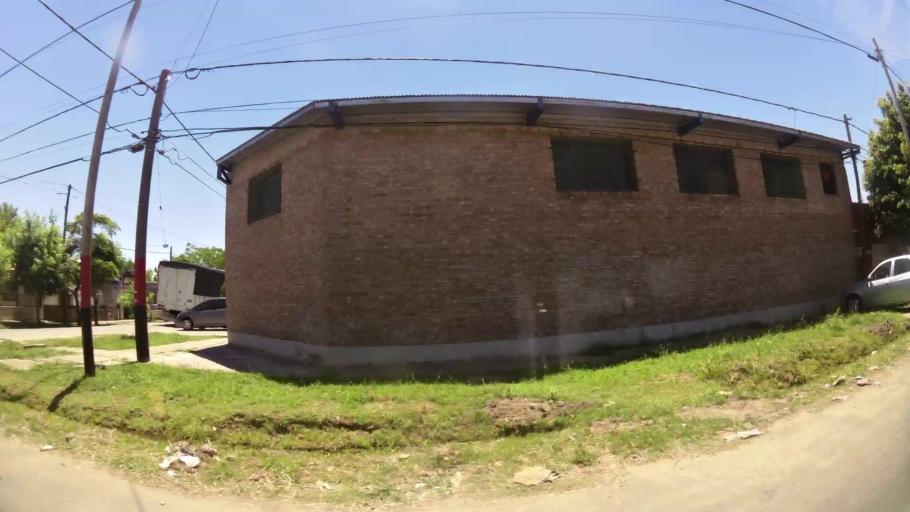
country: AR
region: Santa Fe
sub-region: Departamento de Rosario
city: Rosario
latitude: -32.9499
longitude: -60.6889
